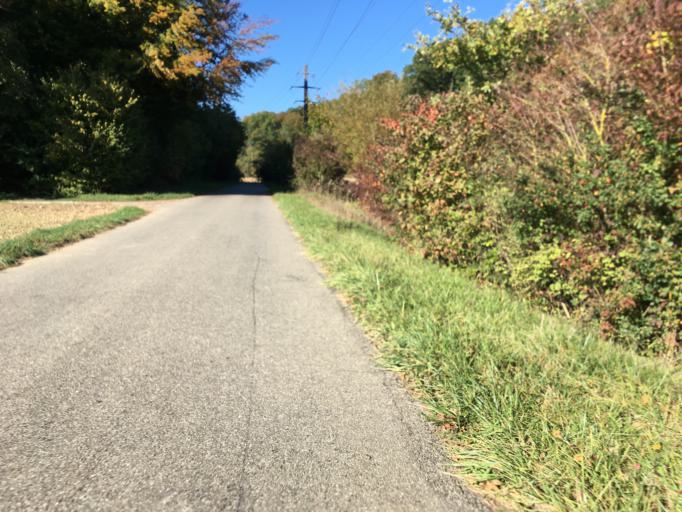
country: CH
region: Zurich
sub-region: Bezirk Buelach
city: Buelach / Soligaenter
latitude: 47.5369
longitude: 8.5437
